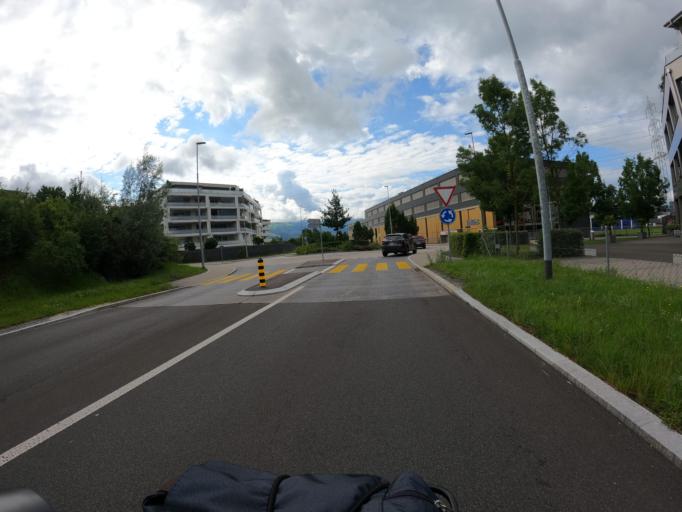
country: CH
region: Zug
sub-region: Zug
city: Steinhausen
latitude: 47.1920
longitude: 8.4831
